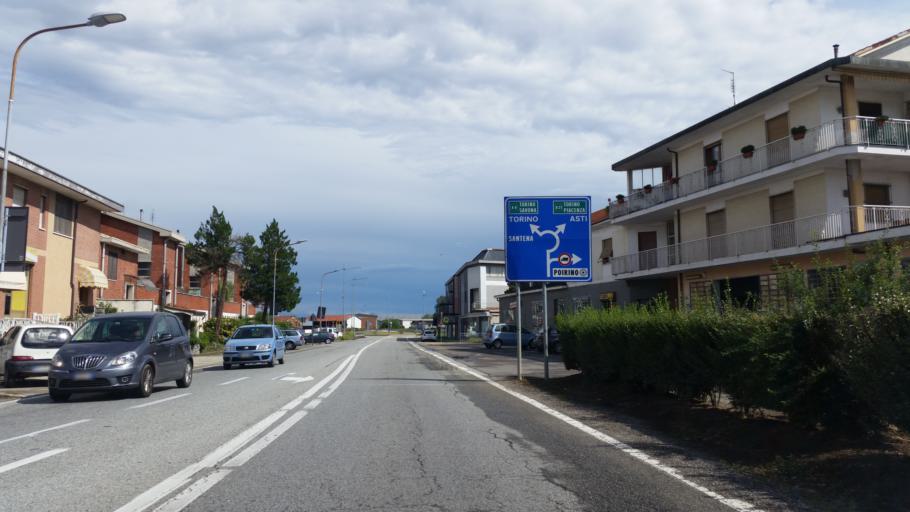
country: IT
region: Piedmont
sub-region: Provincia di Torino
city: Poirino
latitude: 44.9225
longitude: 7.8379
